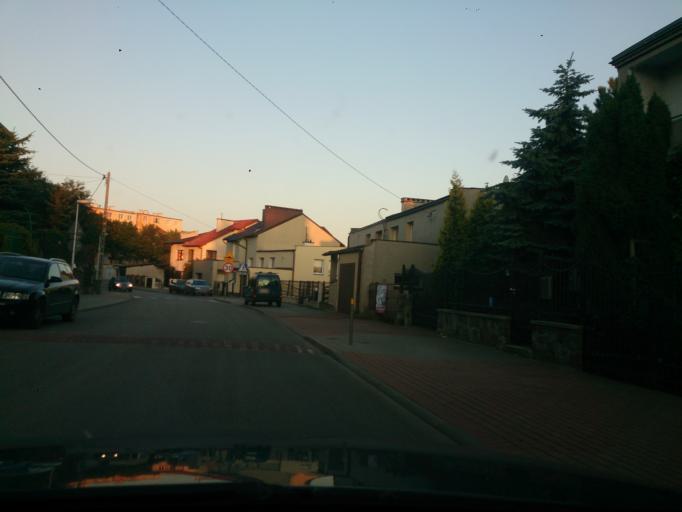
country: PL
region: Pomeranian Voivodeship
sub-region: Gdynia
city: Gdynia
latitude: 54.4918
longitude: 18.5508
